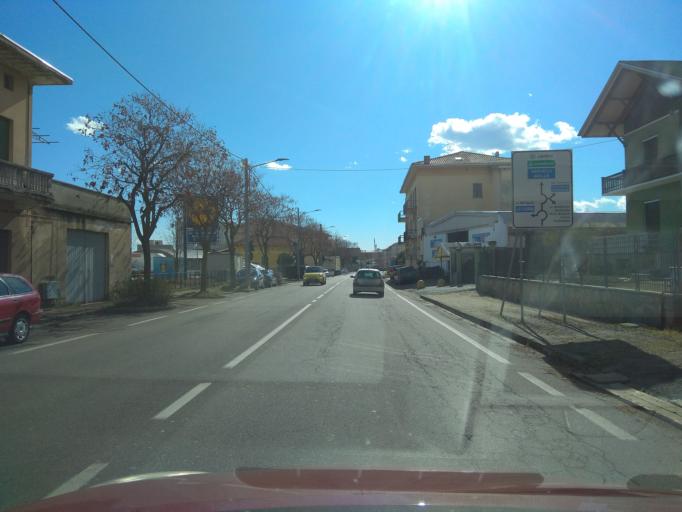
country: IT
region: Piedmont
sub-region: Provincia di Biella
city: Cossato
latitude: 45.5779
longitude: 8.1823
